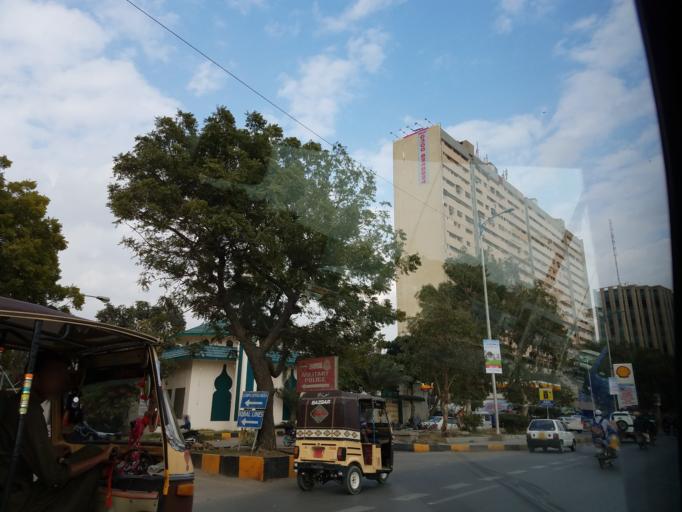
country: PK
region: Sindh
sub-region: Karachi District
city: Karachi
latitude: 24.8568
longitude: 67.0427
